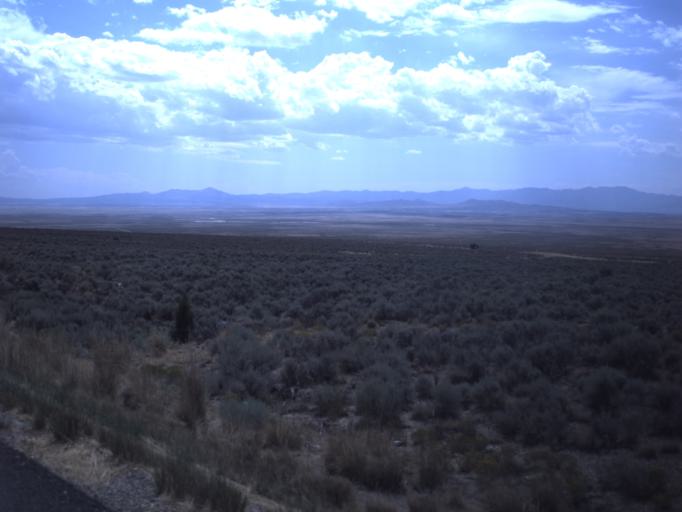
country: US
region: Utah
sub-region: Tooele County
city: Tooele
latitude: 40.3008
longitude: -112.2766
